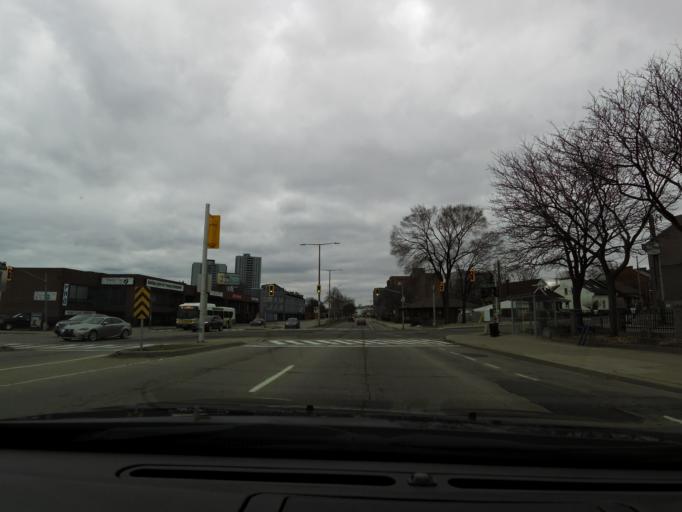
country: CA
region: Ontario
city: Hamilton
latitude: 43.2656
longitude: -79.8819
